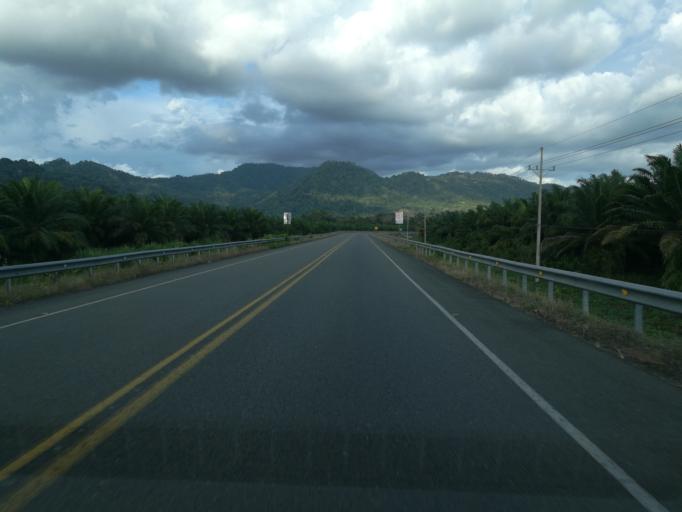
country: CR
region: Puntarenas
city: Quepos
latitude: 9.3707
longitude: -84.0302
